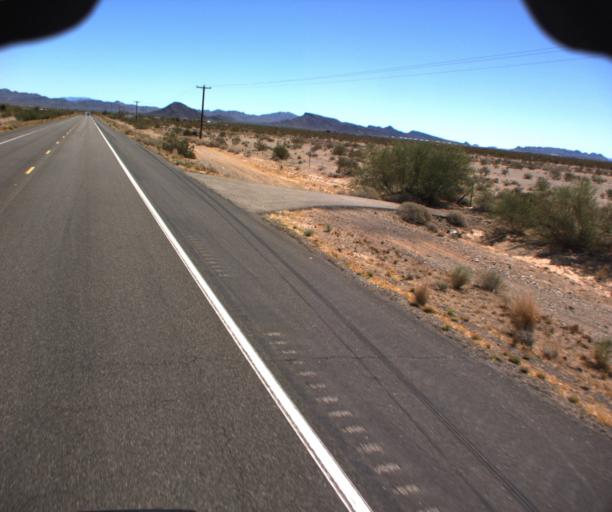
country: US
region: Arizona
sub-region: La Paz County
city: Salome
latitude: 33.7084
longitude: -113.8189
